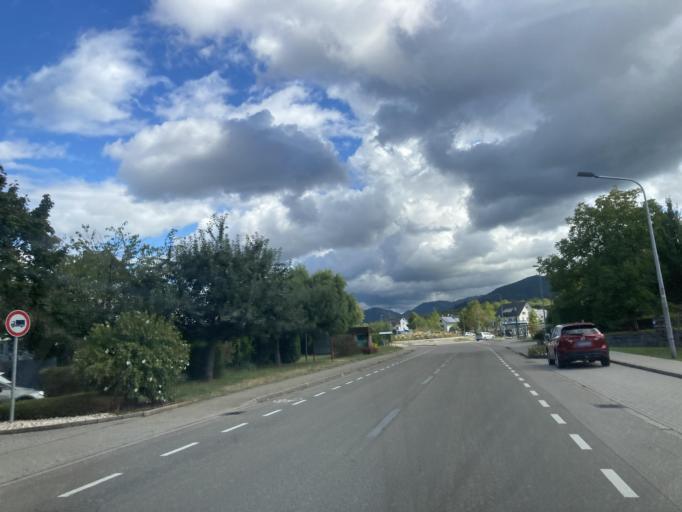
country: DE
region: Baden-Wuerttemberg
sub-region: Karlsruhe Region
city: Ottersweier
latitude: 48.6719
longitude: 8.1167
